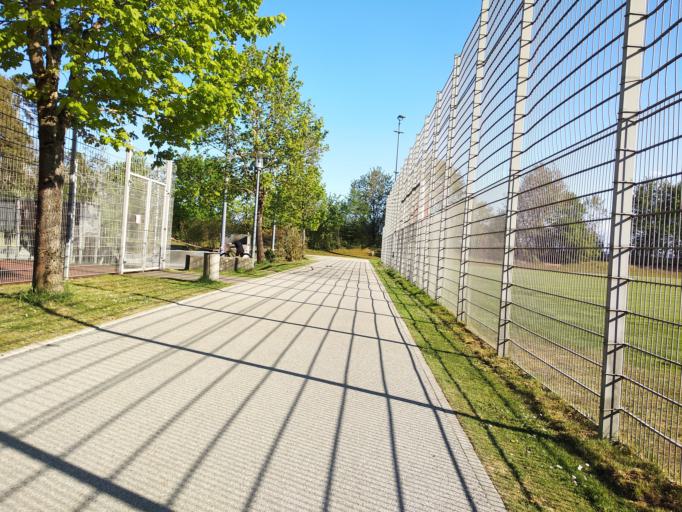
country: DE
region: Bavaria
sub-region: Upper Bavaria
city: Grasbrunn
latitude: 48.0882
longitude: 11.7539
